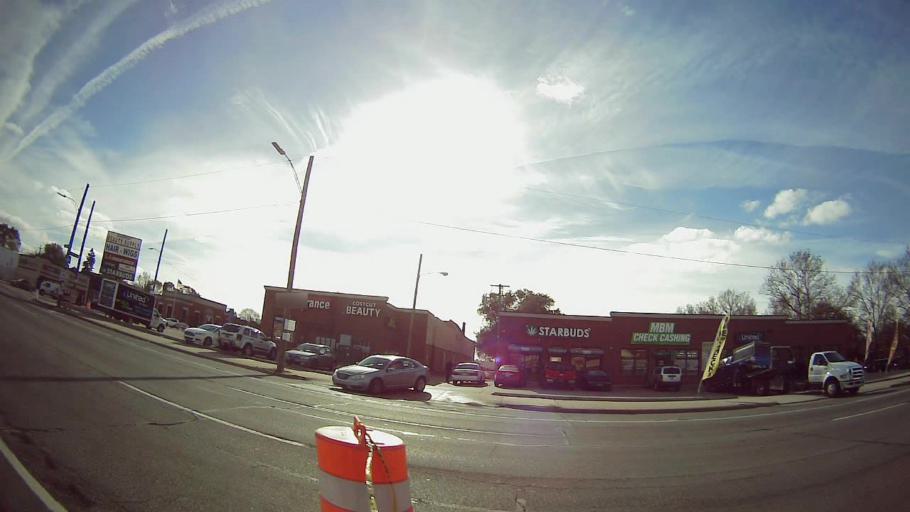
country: US
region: Michigan
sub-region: Macomb County
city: Warren
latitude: 42.4482
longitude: -83.0255
